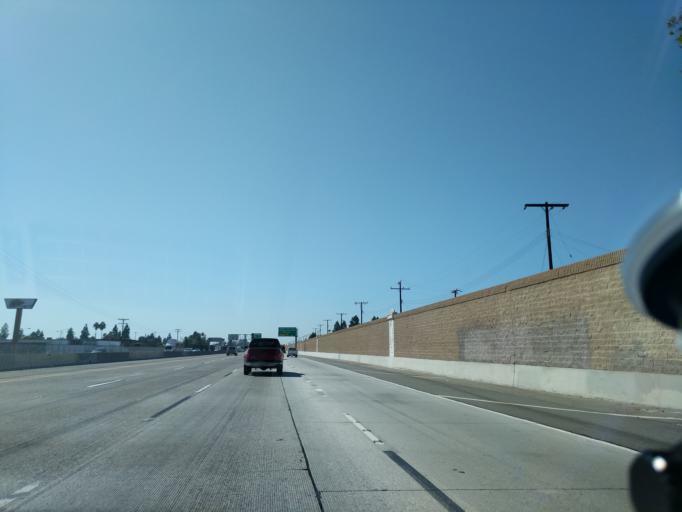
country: US
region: California
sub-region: Orange County
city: Westminster
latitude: 33.7744
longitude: -118.0204
